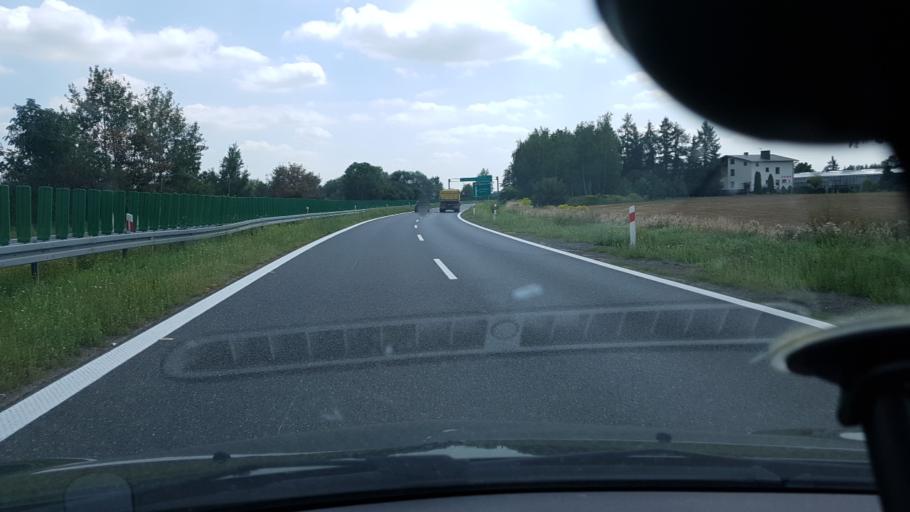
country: PL
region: Silesian Voivodeship
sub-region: Powiat bierunsko-ledzinski
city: Bierun
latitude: 50.1062
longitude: 19.0914
